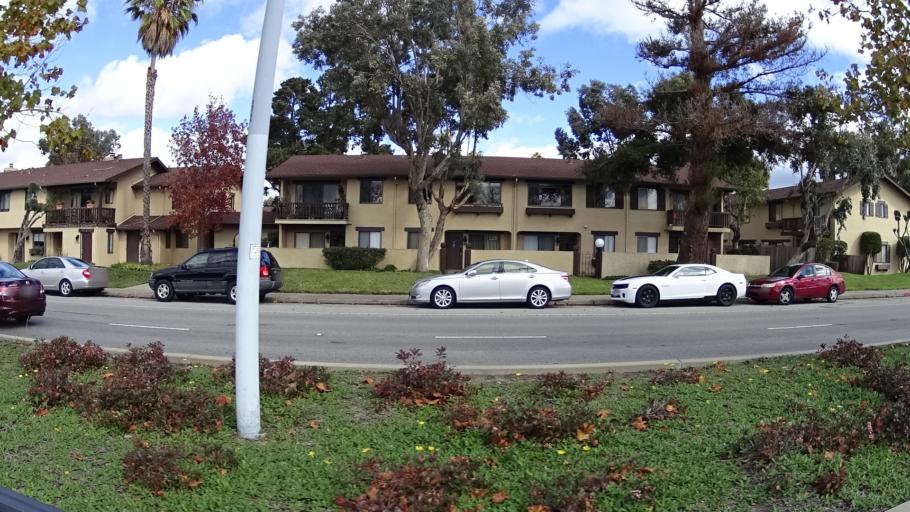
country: US
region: California
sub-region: San Mateo County
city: Foster City
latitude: 37.5574
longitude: -122.2620
